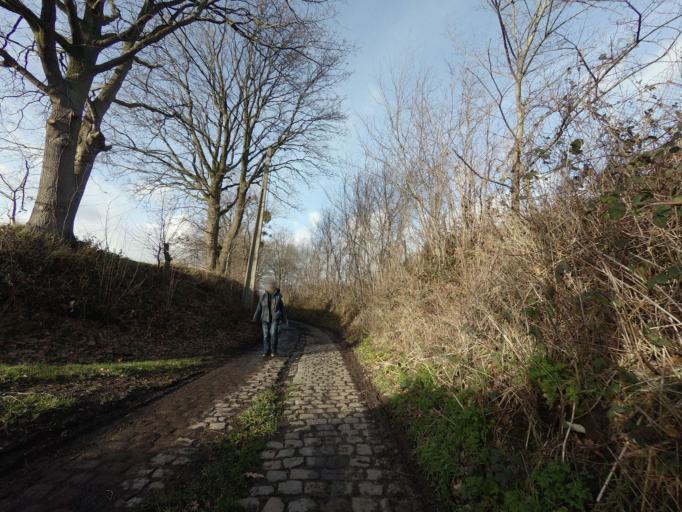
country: BE
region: Flanders
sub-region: Provincie Vlaams-Brabant
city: Bertem
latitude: 50.8824
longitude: 4.6052
